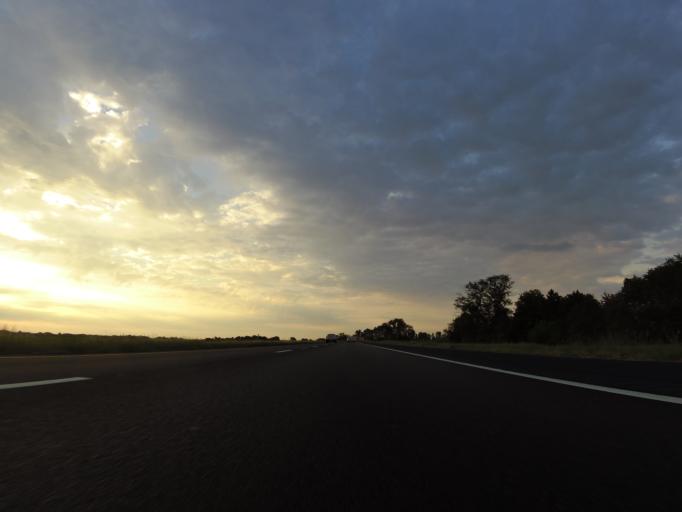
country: US
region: Kansas
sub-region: Sedgwick County
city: Maize
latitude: 37.8070
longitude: -97.4986
